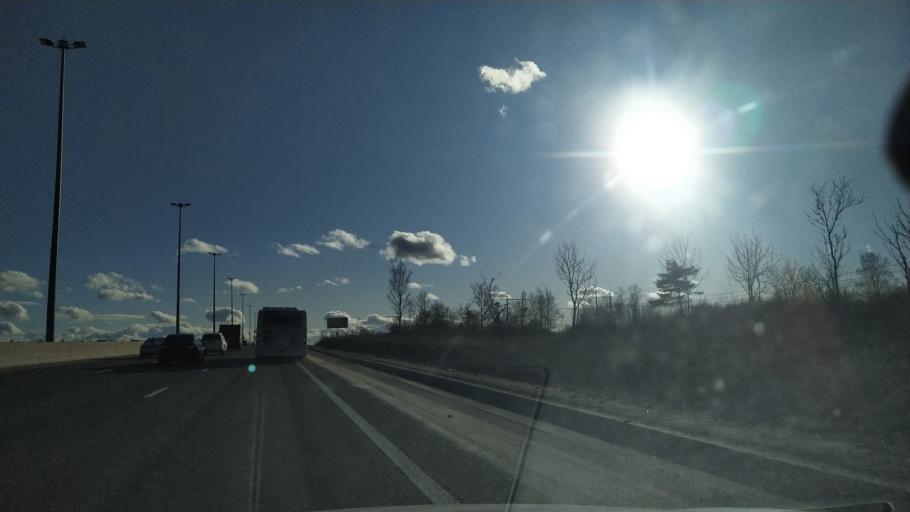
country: RU
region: St.-Petersburg
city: Aleksandrovskaya
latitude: 59.7241
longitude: 30.2884
